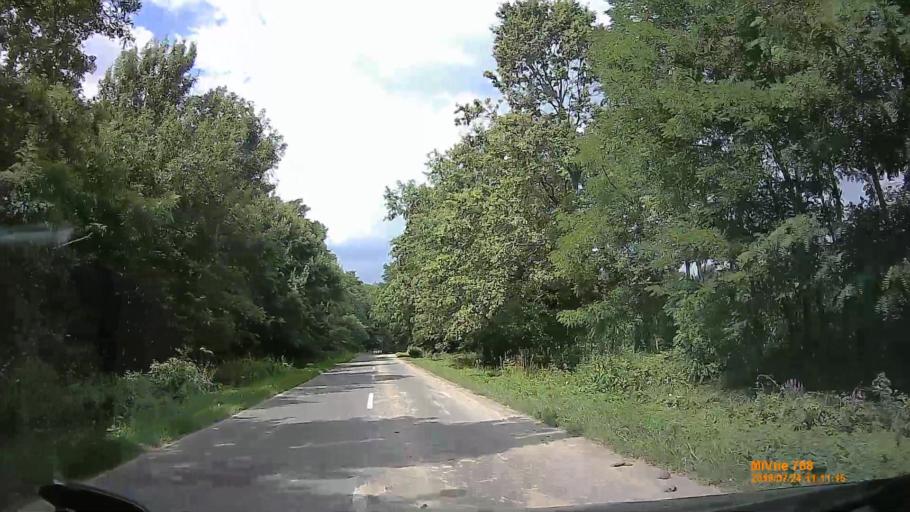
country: HU
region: Szabolcs-Szatmar-Bereg
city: Tarpa
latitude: 48.2022
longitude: 22.4757
